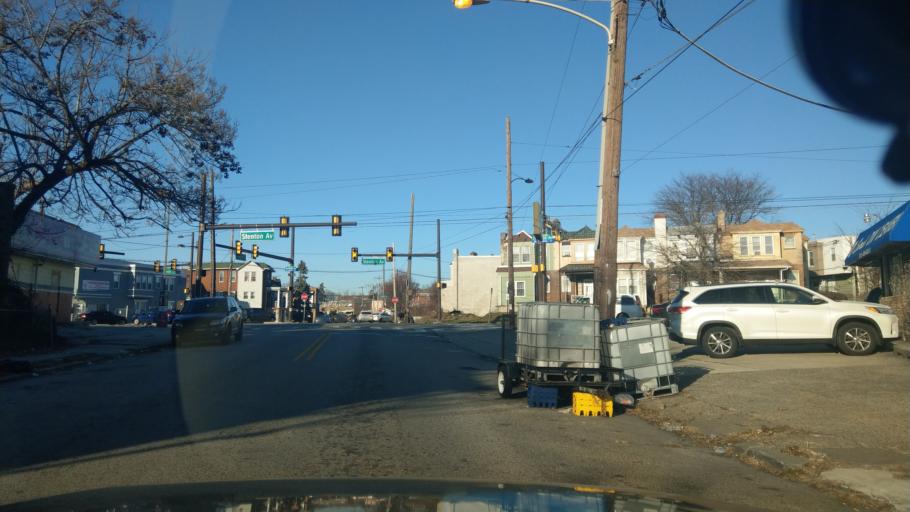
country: US
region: Pennsylvania
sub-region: Montgomery County
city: Wyncote
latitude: 40.0534
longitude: -75.1553
